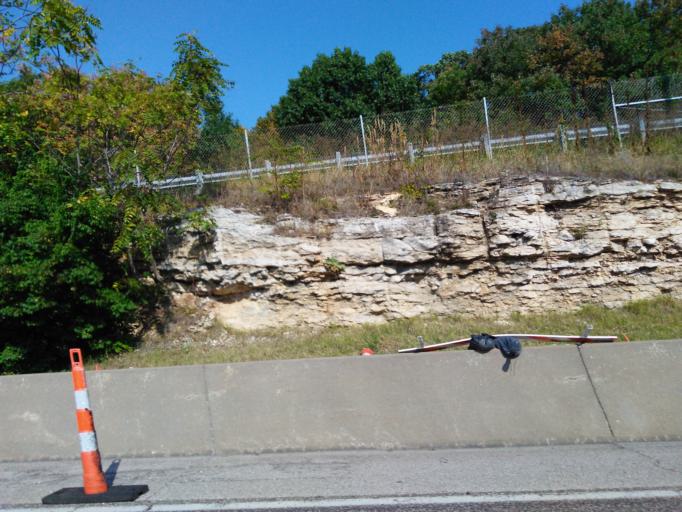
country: US
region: Missouri
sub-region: Saint Louis County
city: Valley Park
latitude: 38.5397
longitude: -90.4838
